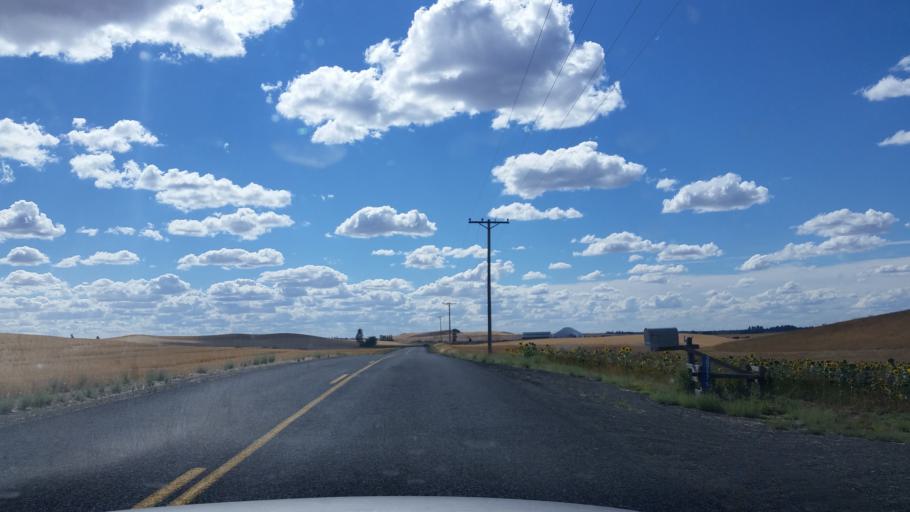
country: US
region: Washington
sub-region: Spokane County
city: Cheney
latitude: 47.3812
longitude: -117.4943
